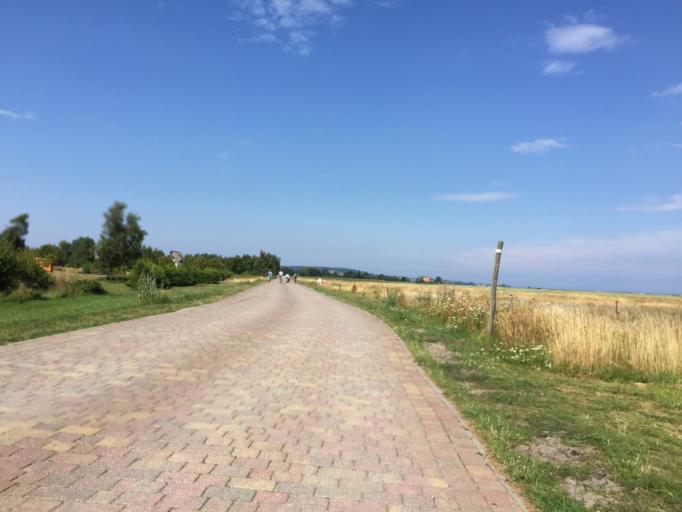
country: DE
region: Mecklenburg-Vorpommern
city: Hiddensee
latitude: 54.5568
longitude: 13.1084
